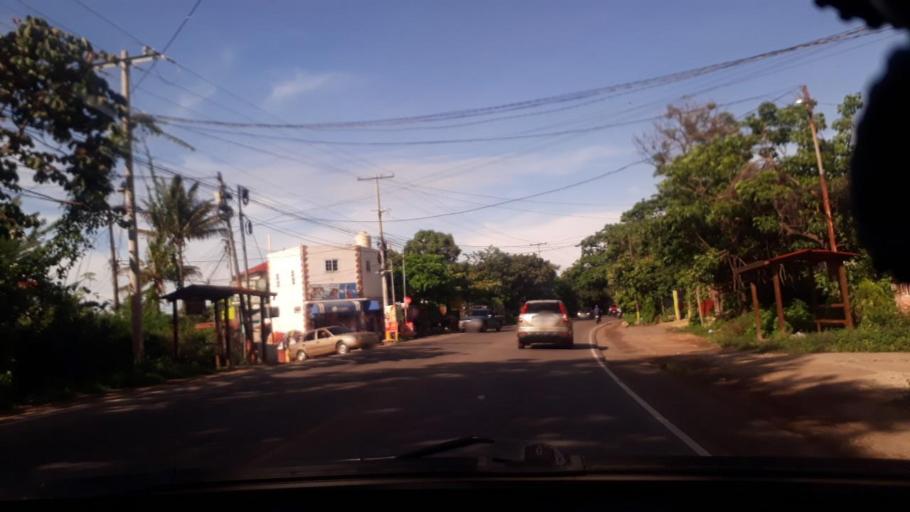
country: GT
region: Jutiapa
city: Jutiapa
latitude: 14.3029
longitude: -89.8720
